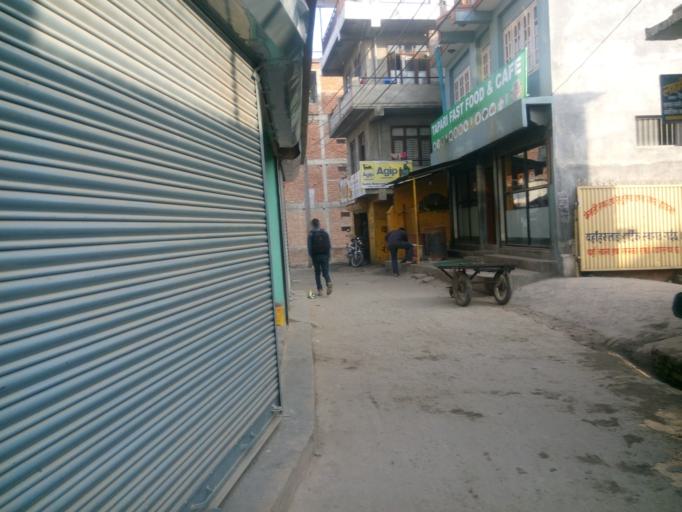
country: NP
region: Central Region
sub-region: Bagmati Zone
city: Patan
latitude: 27.6639
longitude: 85.3357
